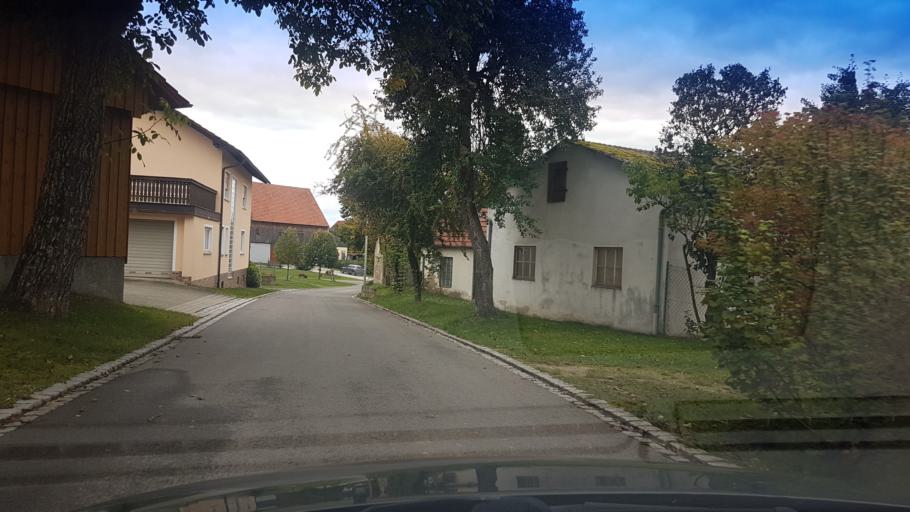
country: DE
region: Bavaria
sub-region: Upper Franconia
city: Stadelhofen
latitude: 50.0076
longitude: 11.2409
